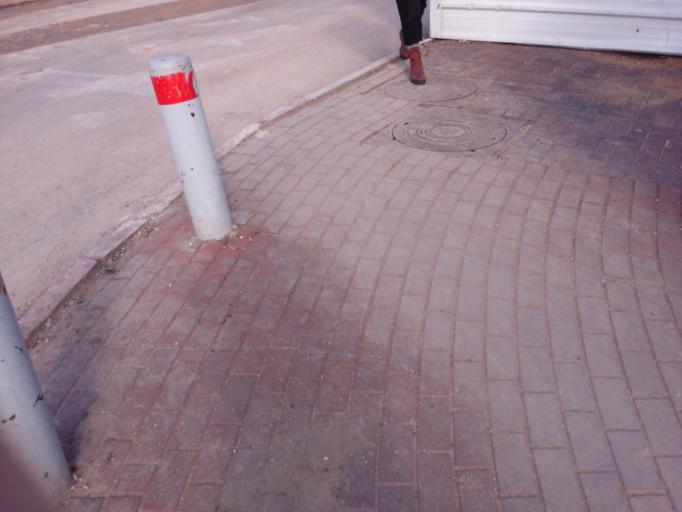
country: IL
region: Tel Aviv
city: Ramat Gan
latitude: 32.0831
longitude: 34.7958
